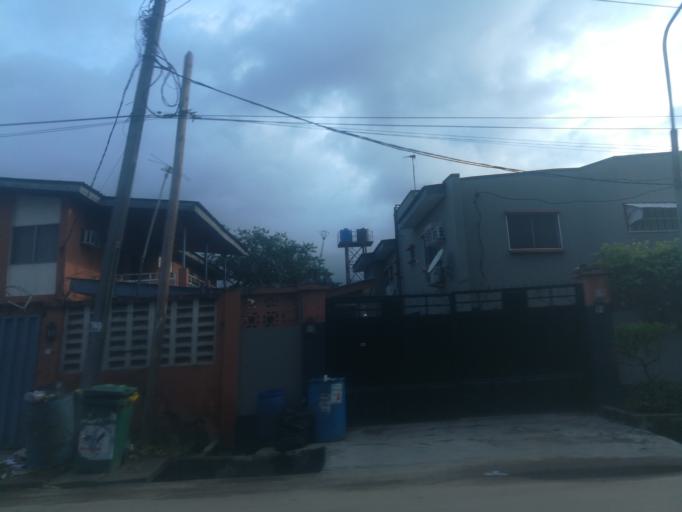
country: NG
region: Lagos
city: Somolu
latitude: 6.5468
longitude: 3.3896
